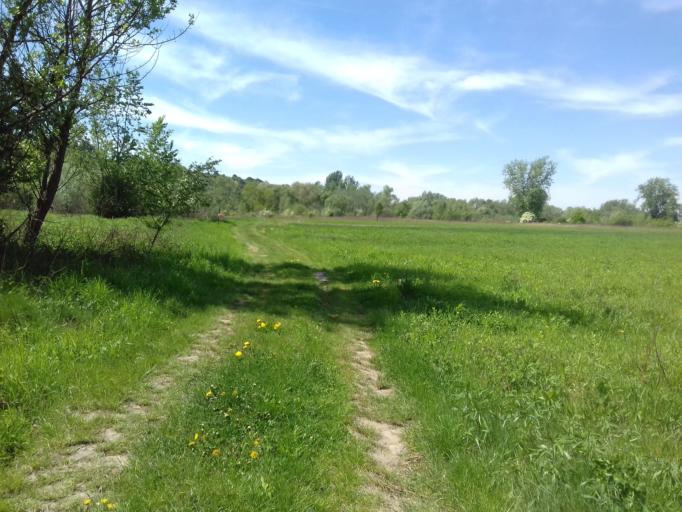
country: PL
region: Lesser Poland Voivodeship
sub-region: Powiat bochenski
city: Stanislawice
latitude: 49.9721
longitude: 20.3328
